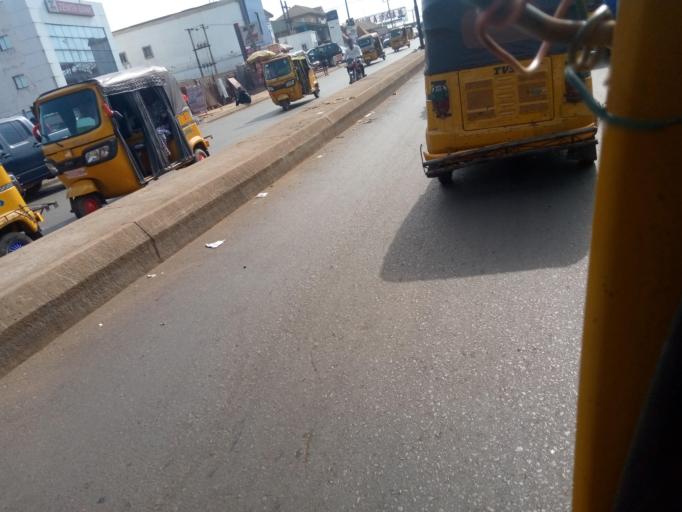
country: NG
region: Enugu
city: Nsukka
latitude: 6.8501
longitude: 7.3962
